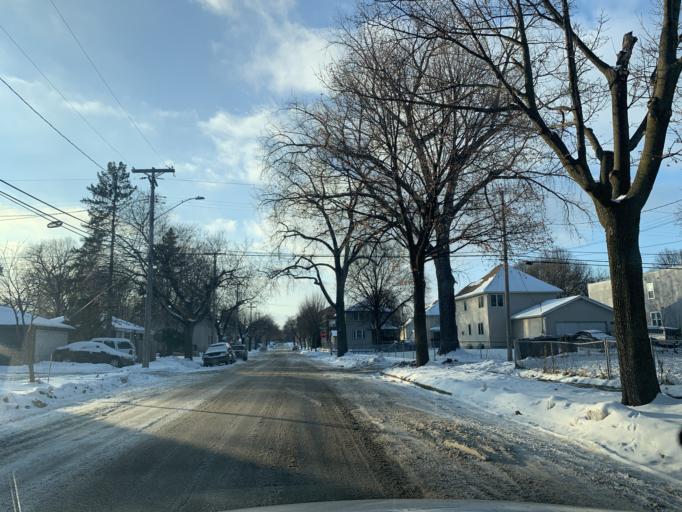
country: US
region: Minnesota
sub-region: Hennepin County
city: Minneapolis
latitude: 44.9879
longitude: -93.3035
